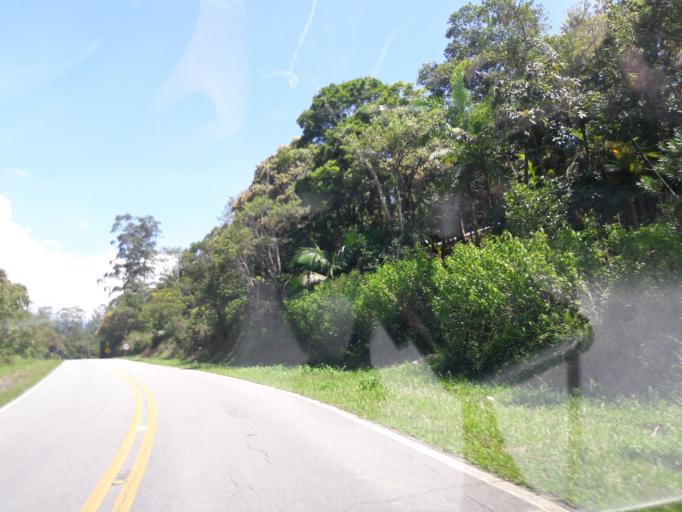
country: BR
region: Parana
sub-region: Antonina
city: Antonina
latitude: -25.5247
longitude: -48.7860
